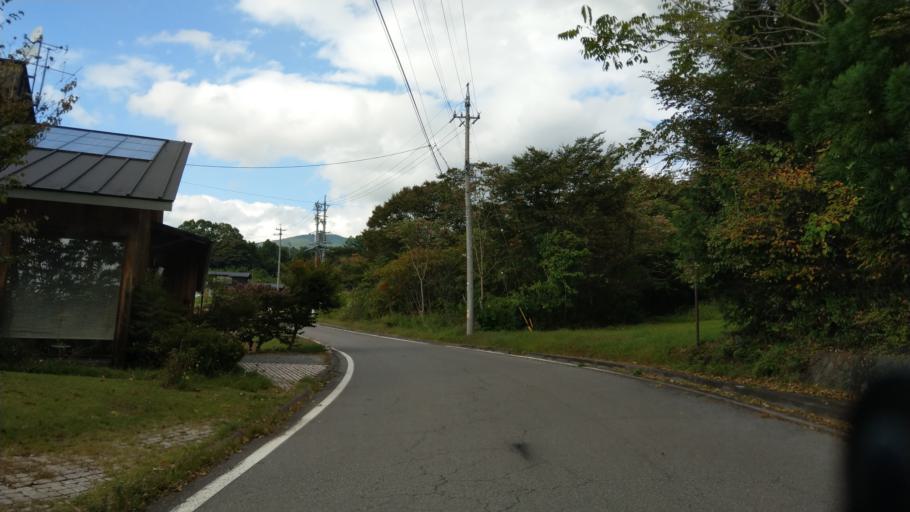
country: JP
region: Nagano
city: Komoro
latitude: 36.3467
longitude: 138.4137
